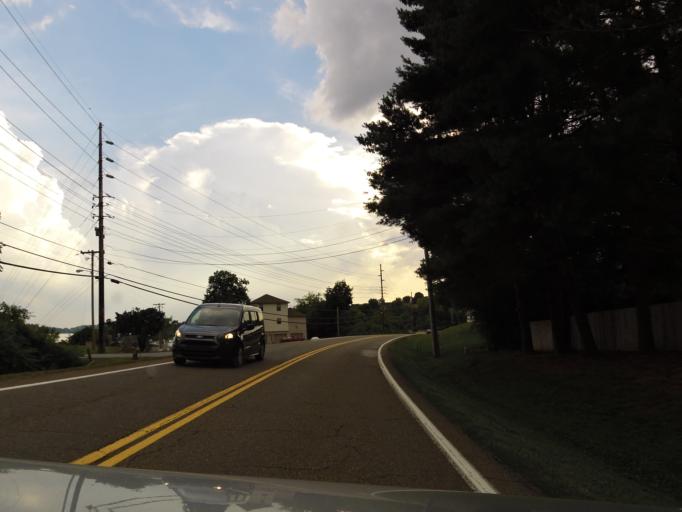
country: US
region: Tennessee
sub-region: Blount County
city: Louisville
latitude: 35.8534
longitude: -84.0950
